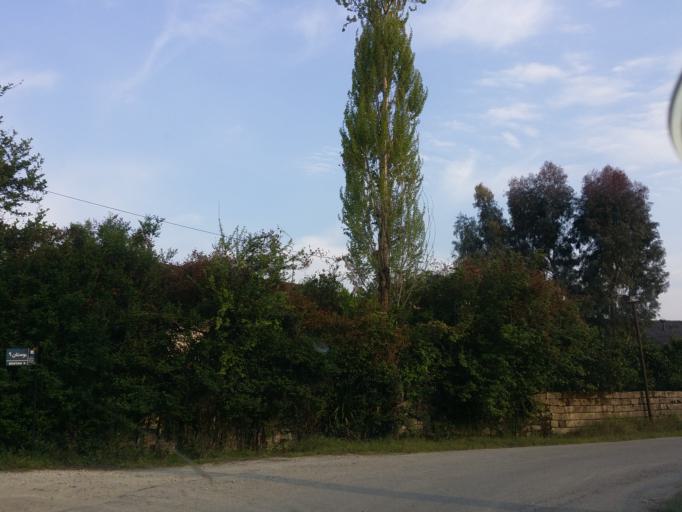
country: IR
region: Mazandaran
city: Chalus
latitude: 36.6721
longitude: 51.3715
